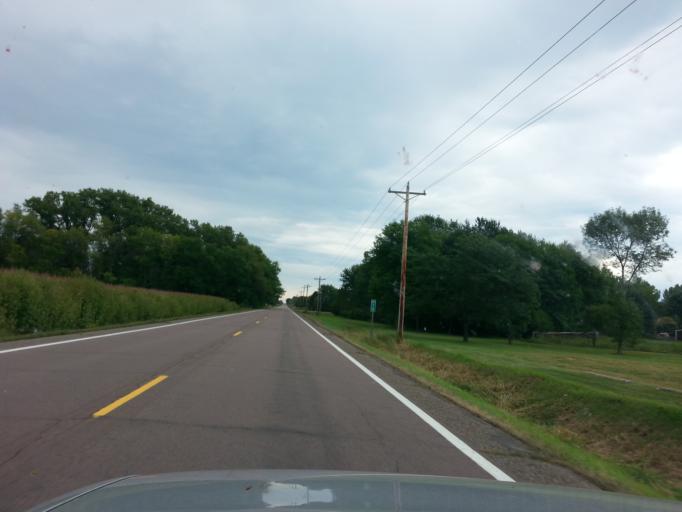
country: US
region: Minnesota
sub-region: Dakota County
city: Farmington
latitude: 44.6305
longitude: -93.1110
